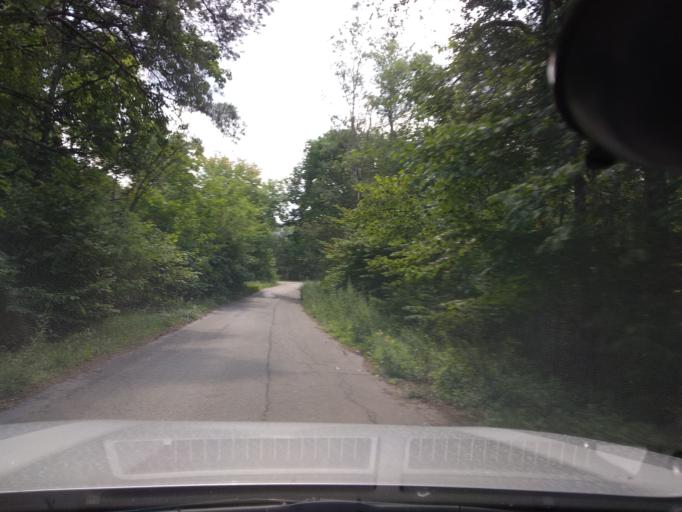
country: LT
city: Grigiskes
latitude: 54.6814
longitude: 25.0789
